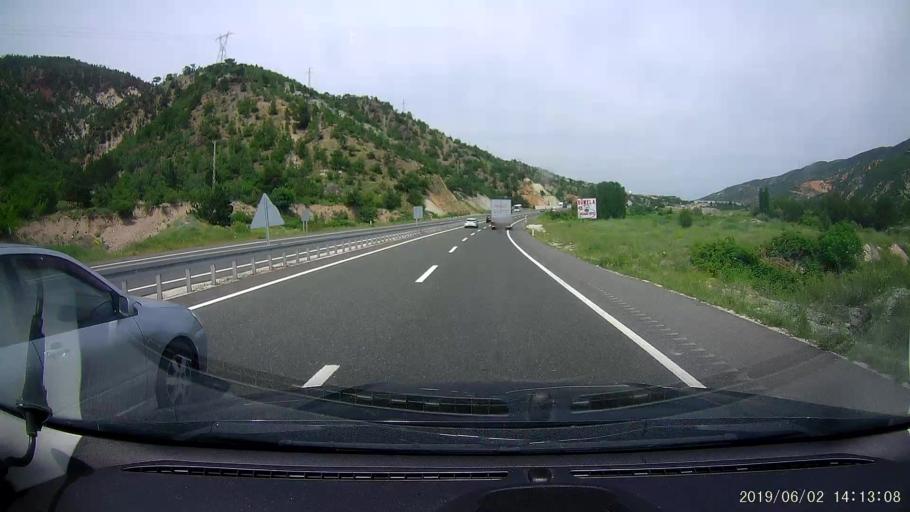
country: TR
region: Cankiri
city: Yaprakli
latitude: 40.9232
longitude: 33.8219
